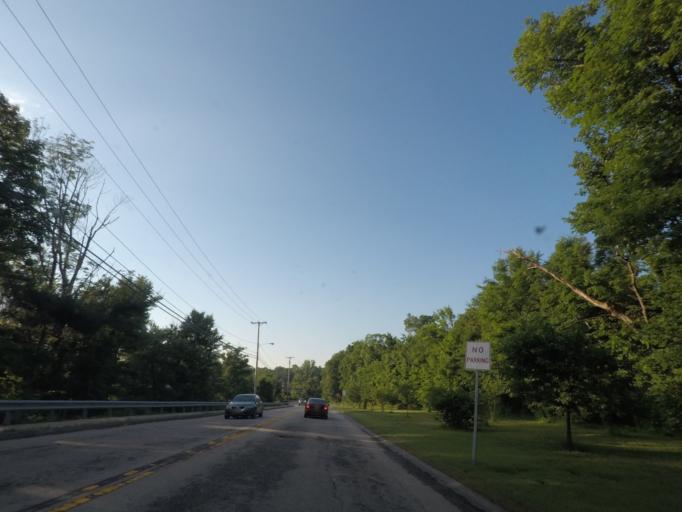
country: US
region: Massachusetts
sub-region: Worcester County
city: Sturbridge
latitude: 42.1033
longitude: -72.0757
